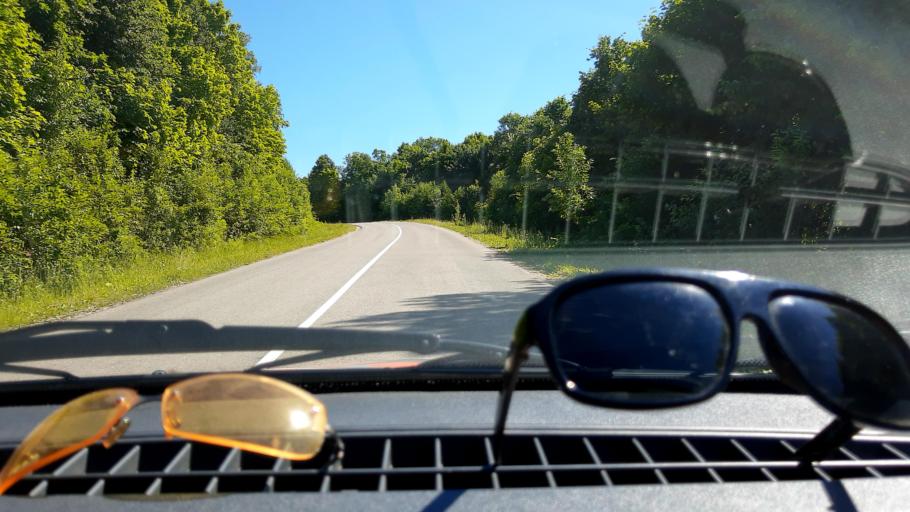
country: RU
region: Bashkortostan
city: Ulu-Telyak
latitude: 54.8195
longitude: 57.0343
